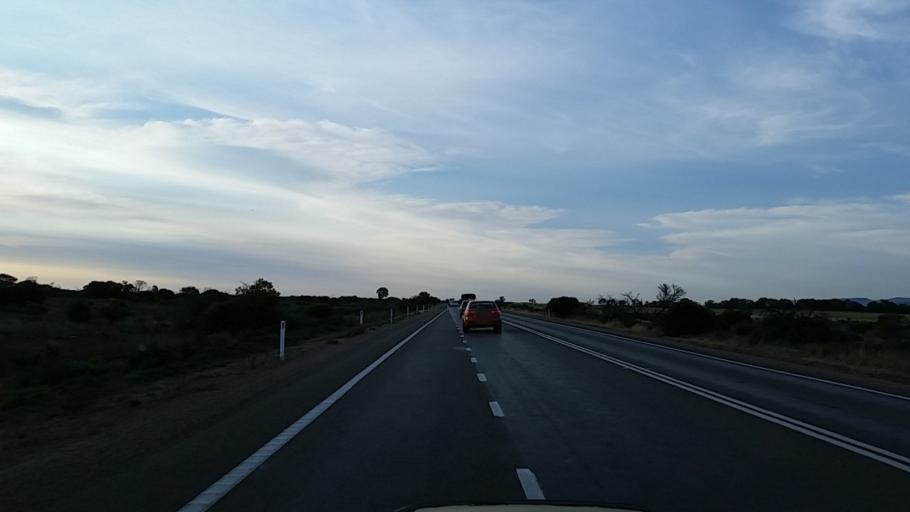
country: AU
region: South Australia
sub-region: Port Pirie City and Dists
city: Port Pirie
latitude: -33.0788
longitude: 138.0481
